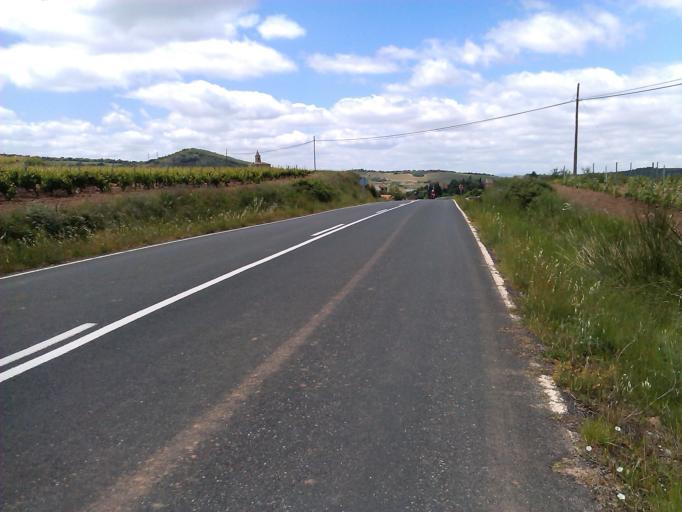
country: ES
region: La Rioja
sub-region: Provincia de La Rioja
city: Ventosa
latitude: 42.4025
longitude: -2.6193
